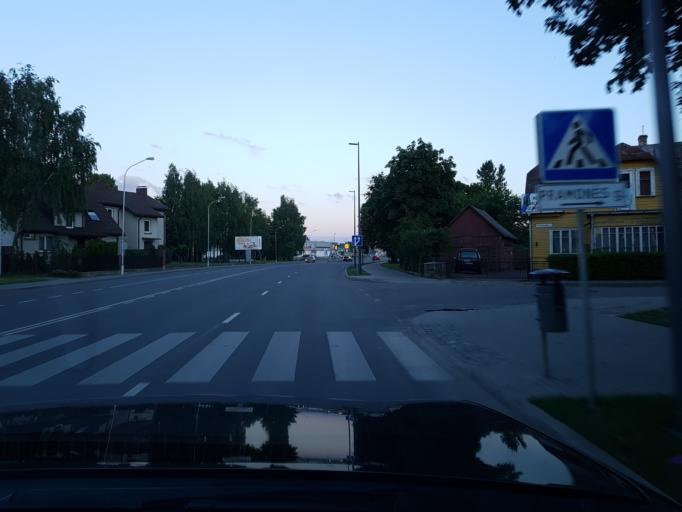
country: LT
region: Marijampoles apskritis
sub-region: Marijampole Municipality
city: Marijampole
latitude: 54.5592
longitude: 23.3539
